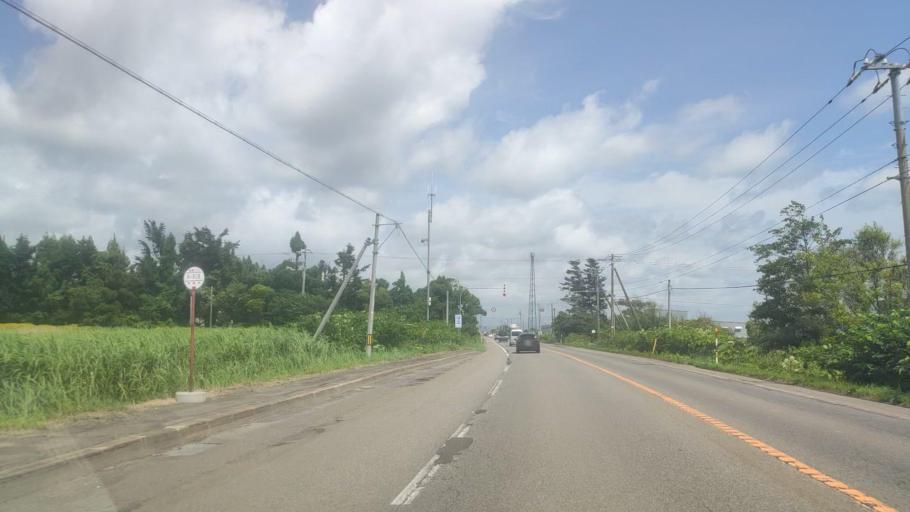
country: JP
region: Hokkaido
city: Niseko Town
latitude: 42.4700
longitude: 140.3429
